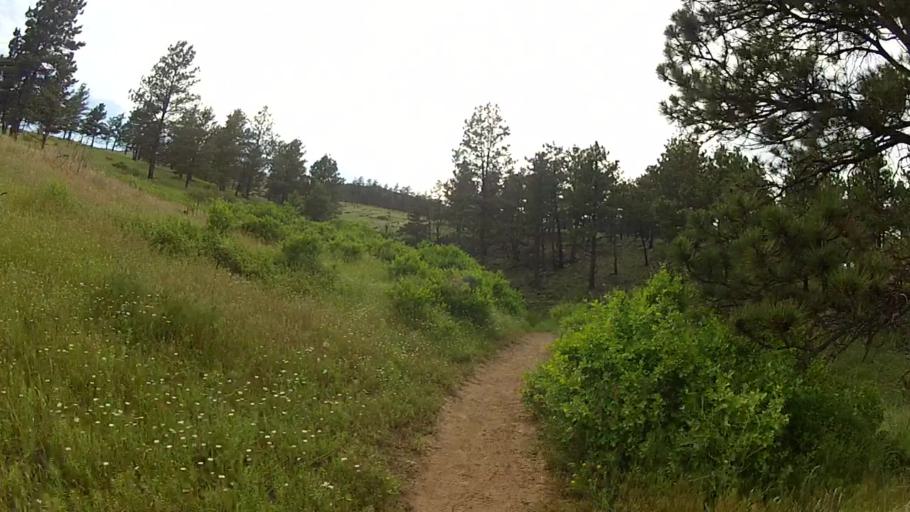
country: US
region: Colorado
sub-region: Larimer County
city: Laporte
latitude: 40.4785
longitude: -105.2358
